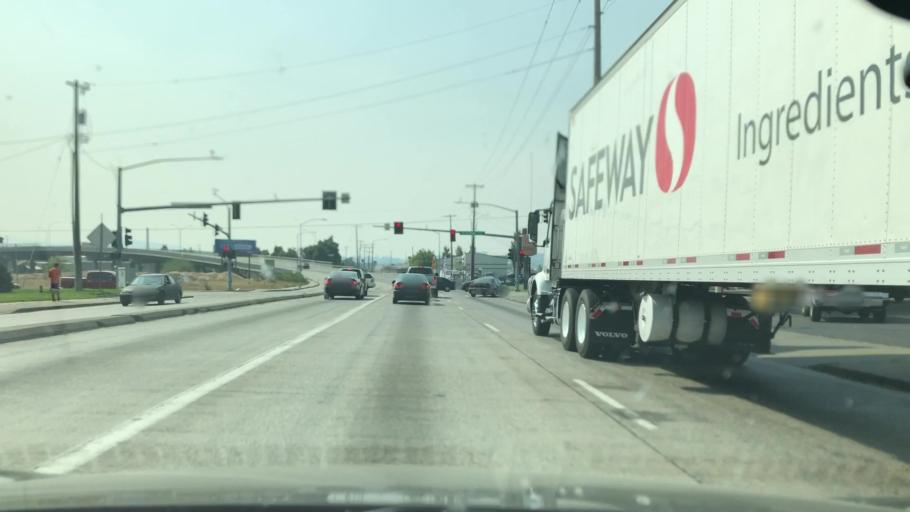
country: US
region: Washington
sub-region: Spokane County
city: Spokane
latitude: 47.6725
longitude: -117.3638
